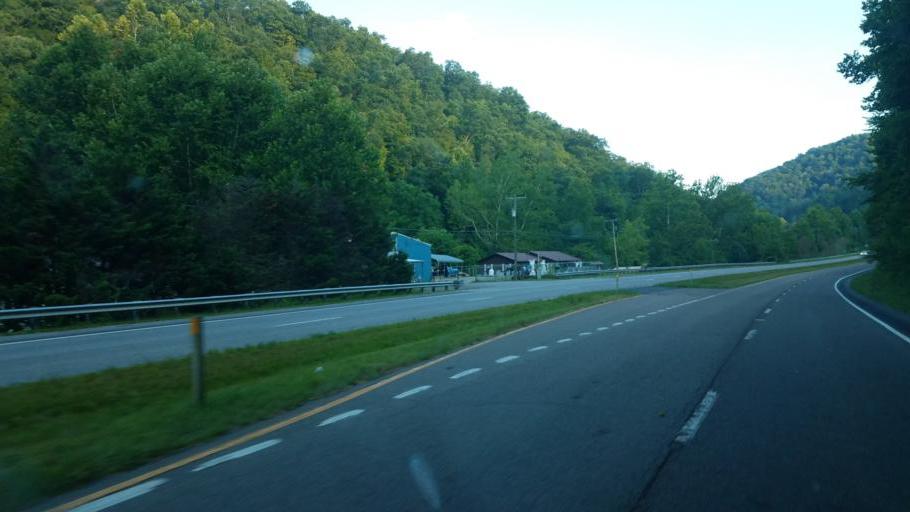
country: US
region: Tennessee
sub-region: Hawkins County
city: Church Hill
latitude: 36.6797
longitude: -82.7555
